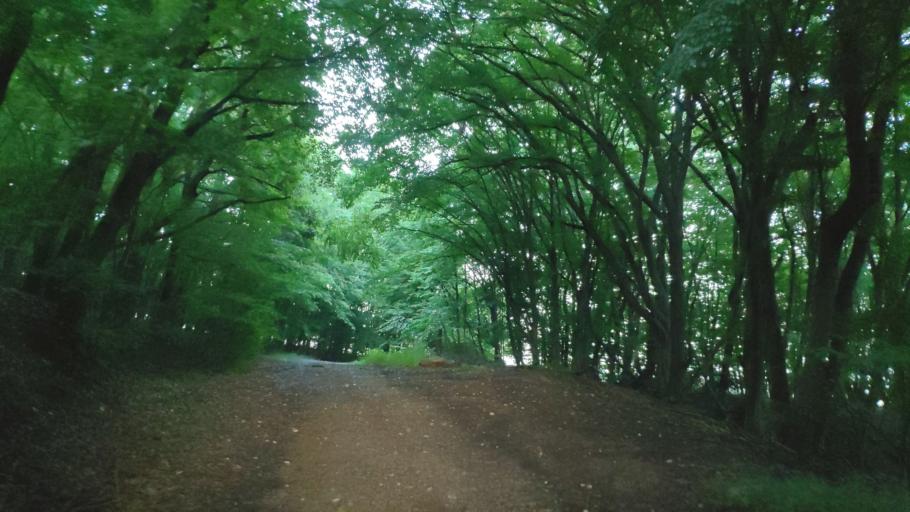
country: SK
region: Kosicky
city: Secovce
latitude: 48.5929
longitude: 21.5349
